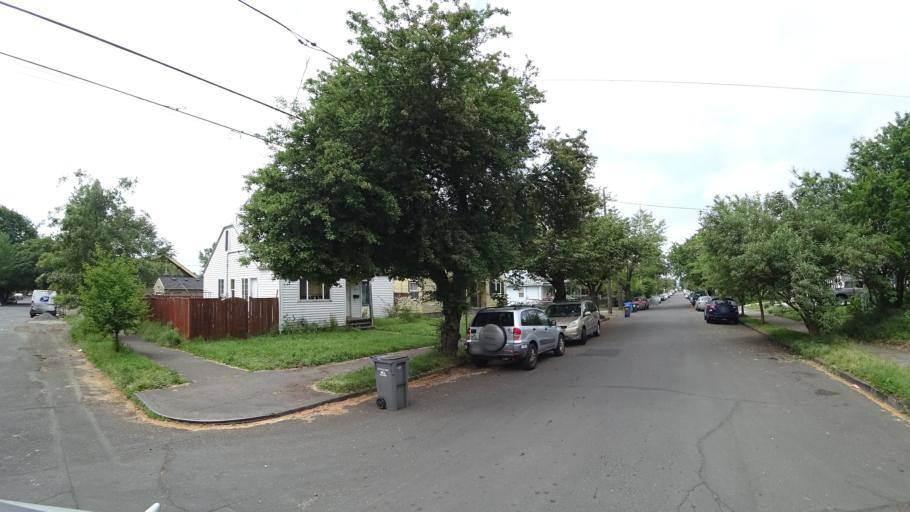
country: US
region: Oregon
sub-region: Multnomah County
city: Portland
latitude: 45.5578
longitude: -122.6488
